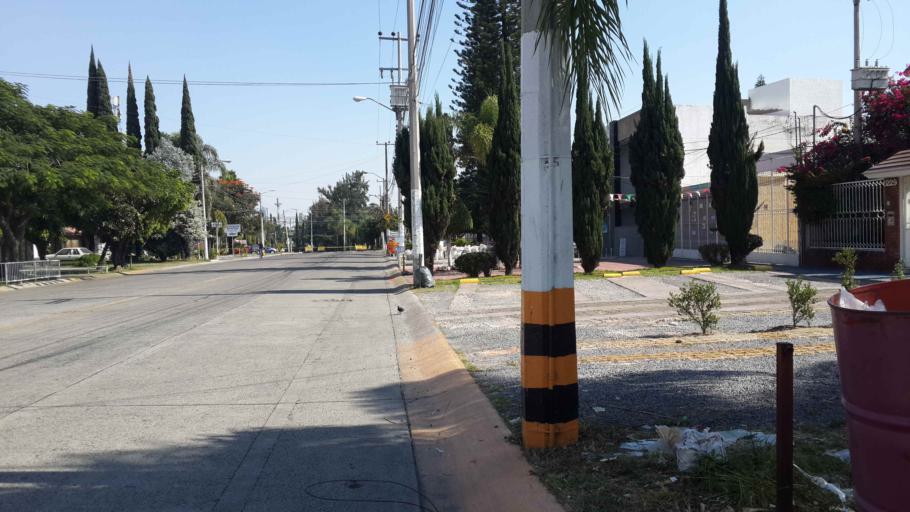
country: MX
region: Jalisco
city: Guadalajara
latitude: 20.6692
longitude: -103.4290
